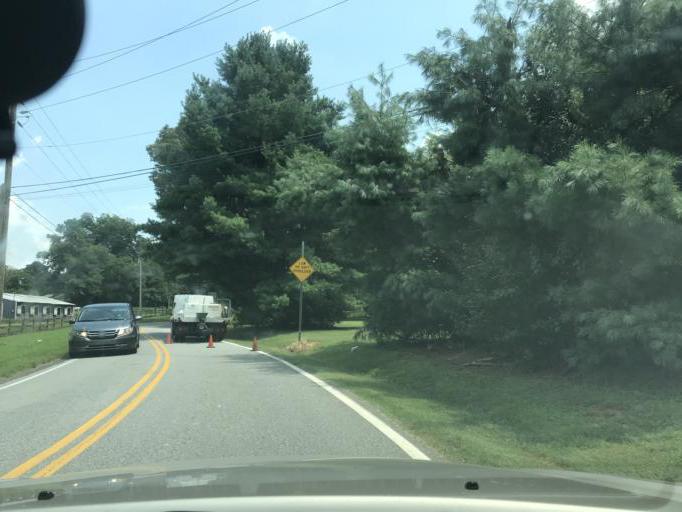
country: US
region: Georgia
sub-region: Forsyth County
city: Cumming
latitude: 34.2712
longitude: -84.1745
